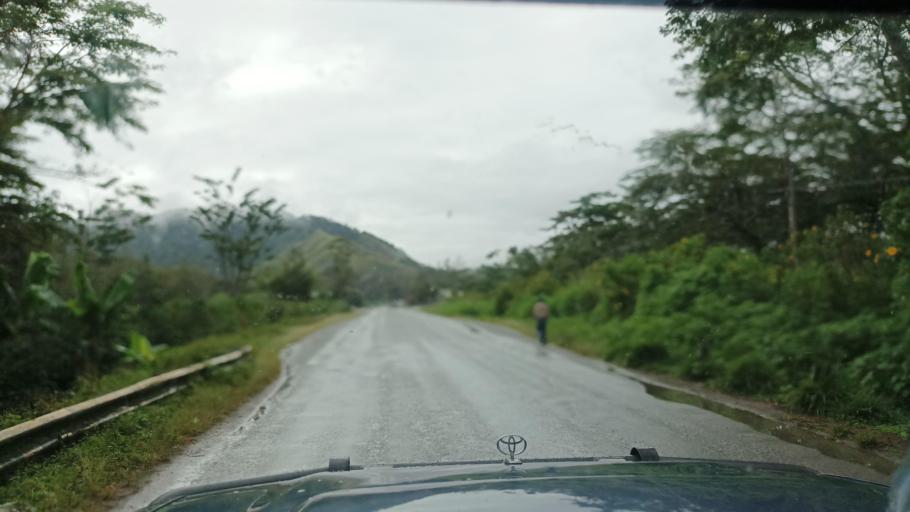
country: PG
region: Western Highlands
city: Rauna
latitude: -5.8341
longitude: 144.3434
